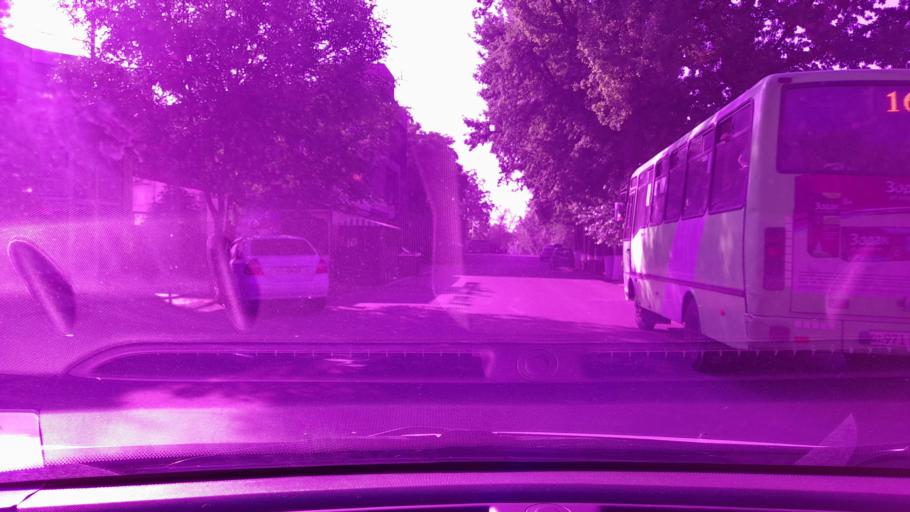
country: UZ
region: Toshkent
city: Salor
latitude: 41.3371
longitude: 69.3563
